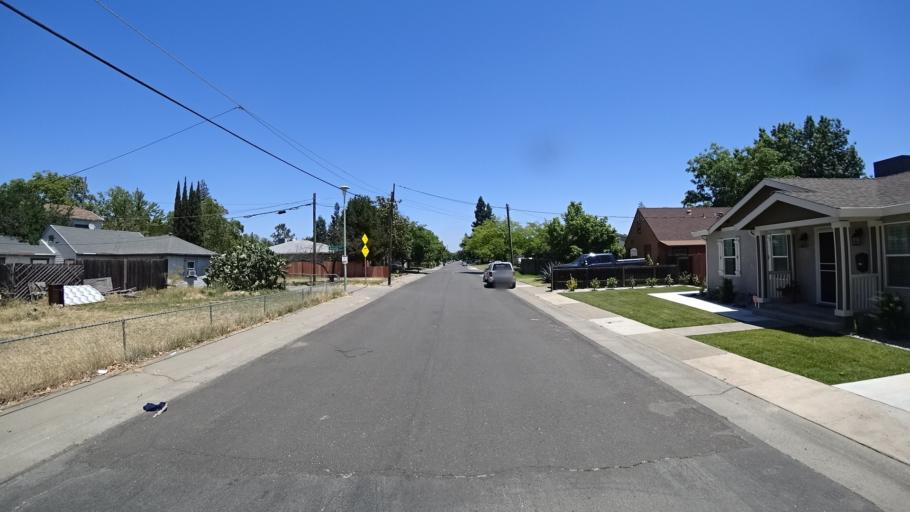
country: US
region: California
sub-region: Sacramento County
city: Sacramento
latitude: 38.5375
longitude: -121.4819
